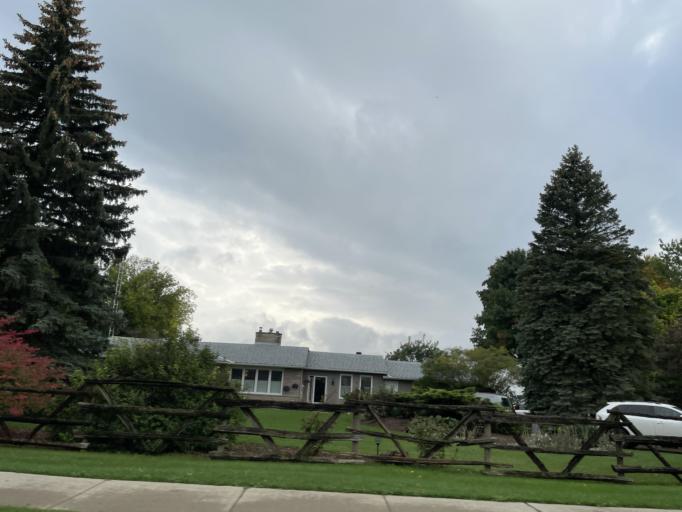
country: CA
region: Ontario
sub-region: Wellington County
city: Guelph
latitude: 43.5297
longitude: -80.1934
